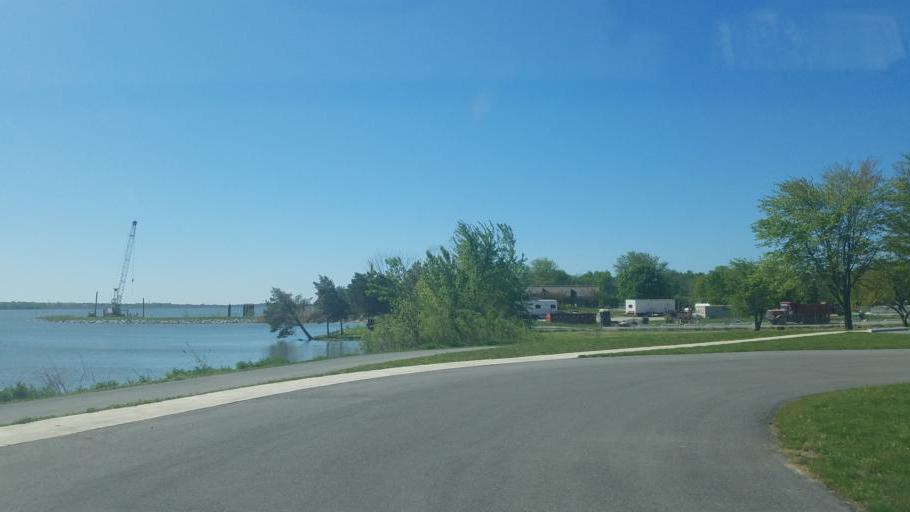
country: US
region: Ohio
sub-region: Delaware County
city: Lewis Center
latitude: 40.2122
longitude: -82.9720
